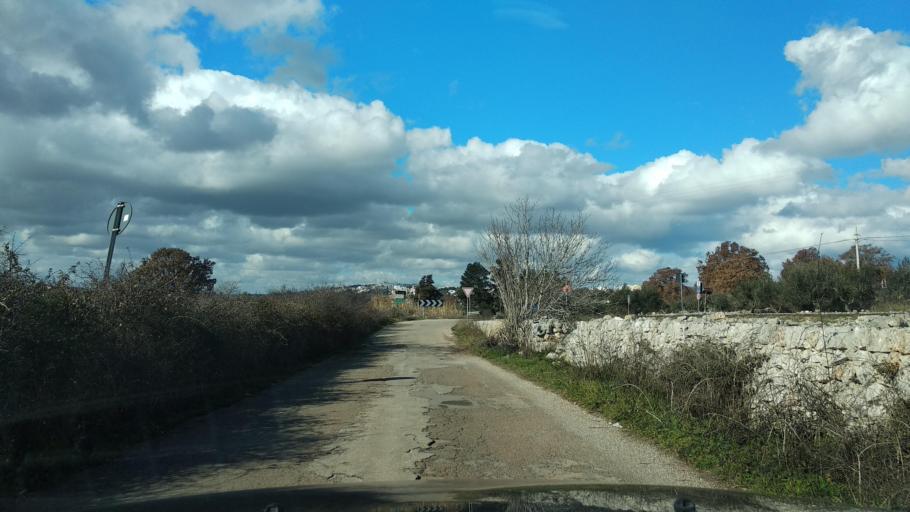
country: IT
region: Apulia
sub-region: Provincia di Brindisi
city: Cisternino
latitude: 40.7228
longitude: 17.4458
